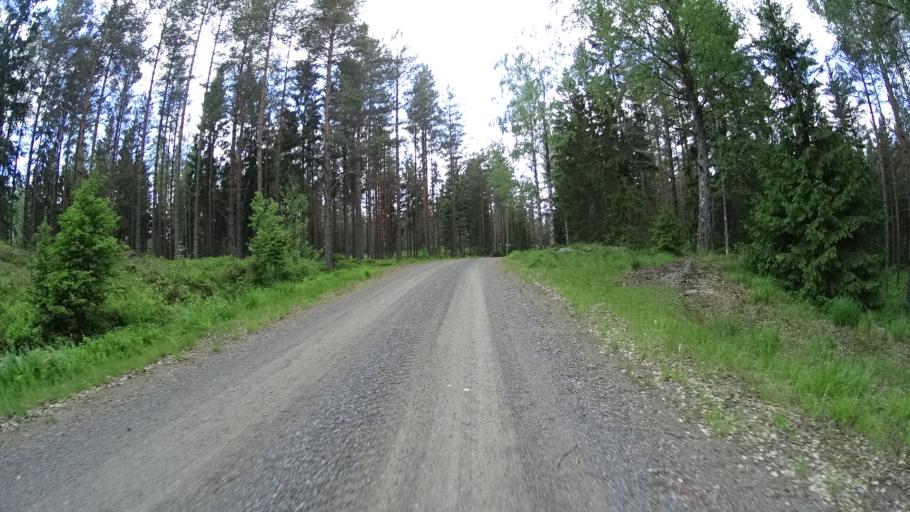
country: FI
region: Uusimaa
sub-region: Raaseporin
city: Pohja
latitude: 60.1801
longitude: 23.5573
